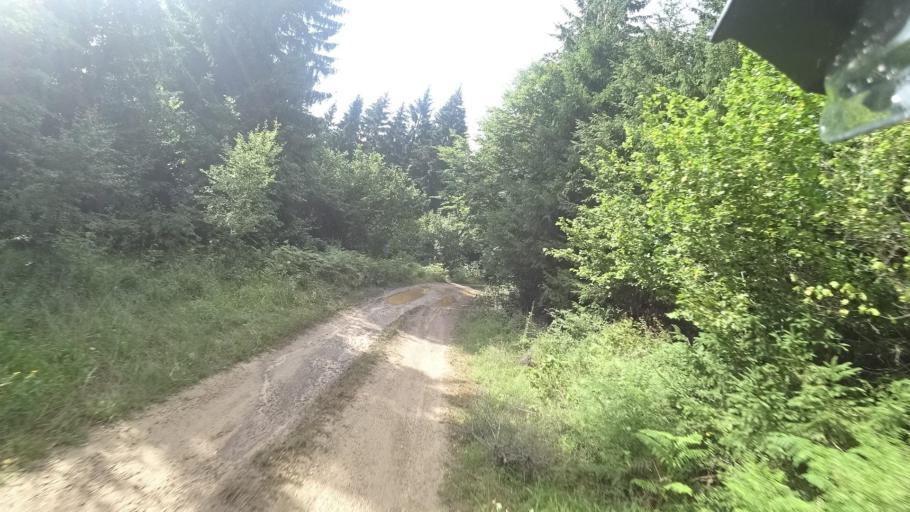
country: HR
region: Licko-Senjska
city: Jezerce
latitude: 44.7722
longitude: 15.6478
